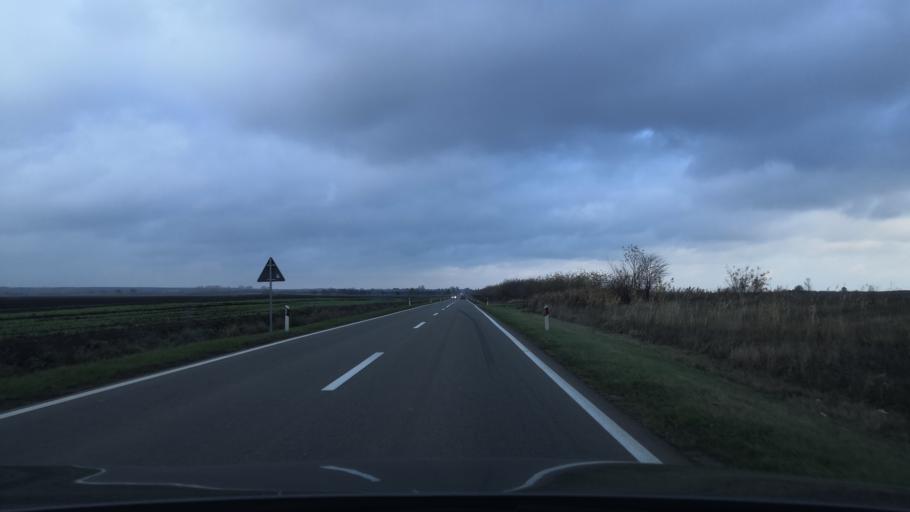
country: RS
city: Sanad
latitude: 46.0060
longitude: 20.1006
